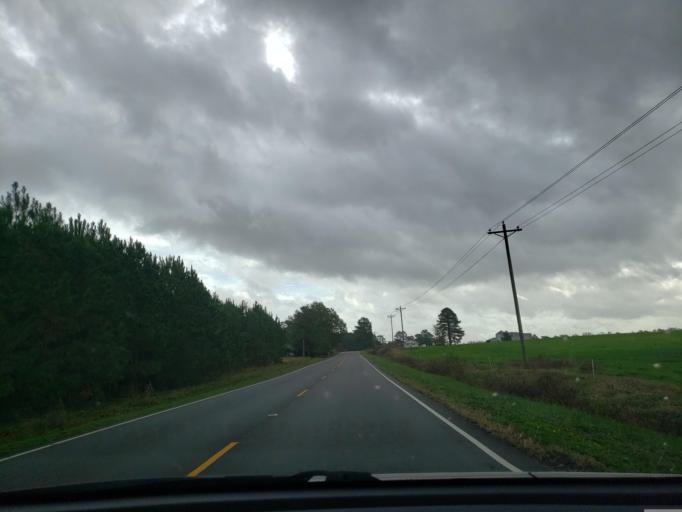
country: US
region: North Carolina
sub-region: Duplin County
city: Beulaville
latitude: 34.8586
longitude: -77.8767
